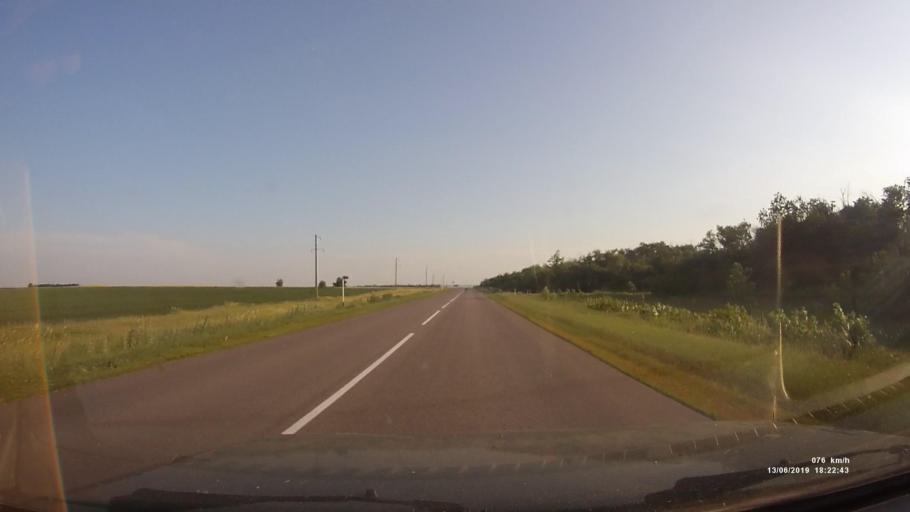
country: RU
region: Rostov
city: Kazanskaya
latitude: 49.8556
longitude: 41.2764
